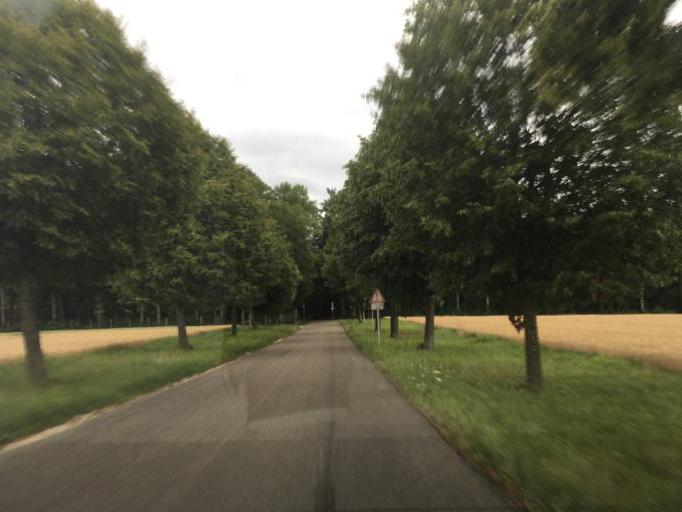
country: DE
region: Baden-Wuerttemberg
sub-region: Tuebingen Region
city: Kirchentellinsfurt
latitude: 48.5459
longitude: 9.1350
